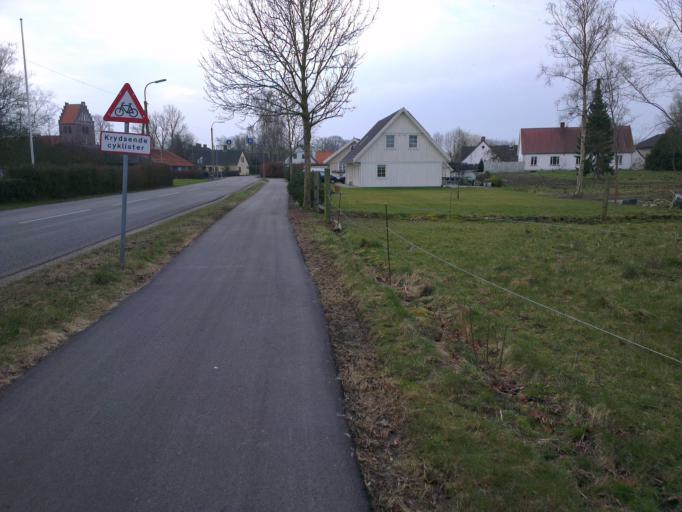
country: DK
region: Capital Region
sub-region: Frederikssund Kommune
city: Skibby
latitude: 55.7627
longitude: 11.9112
